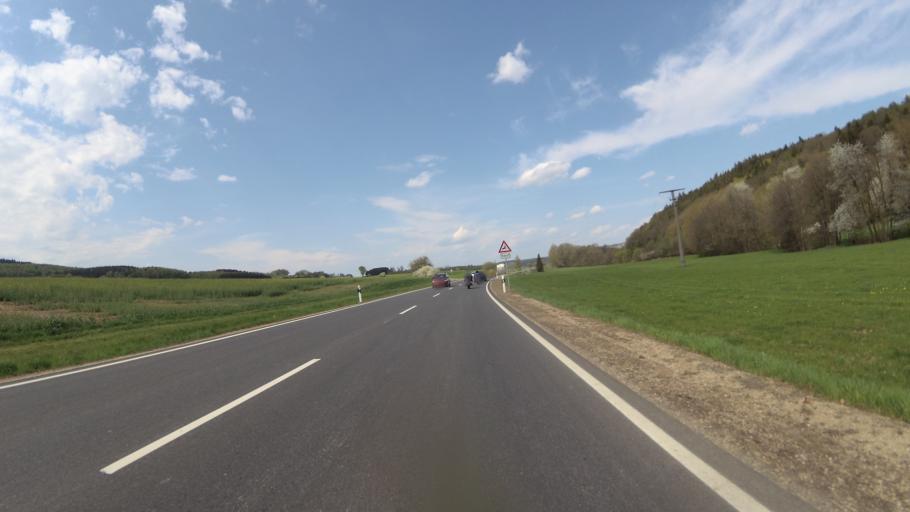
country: DE
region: Rheinland-Pfalz
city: Kelberg
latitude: 50.3016
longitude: 6.9133
